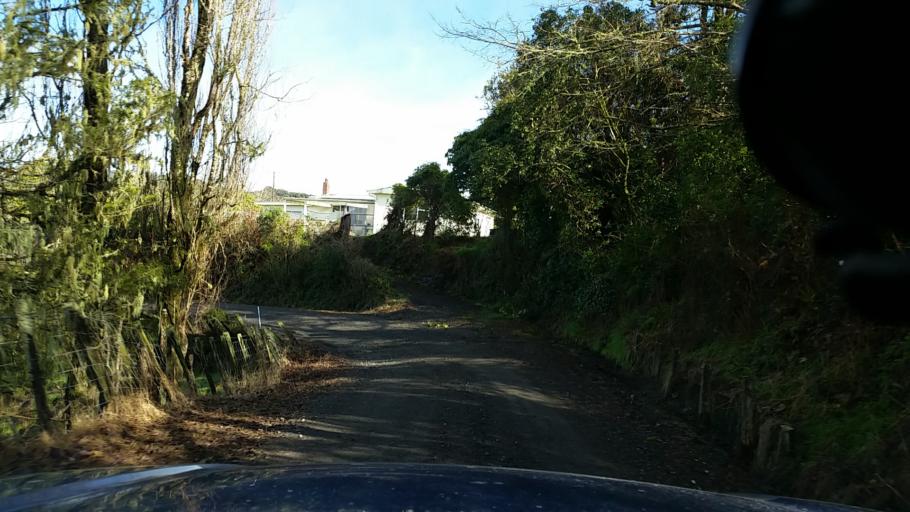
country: NZ
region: Taranaki
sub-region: New Plymouth District
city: Waitara
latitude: -39.0333
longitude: 174.7849
